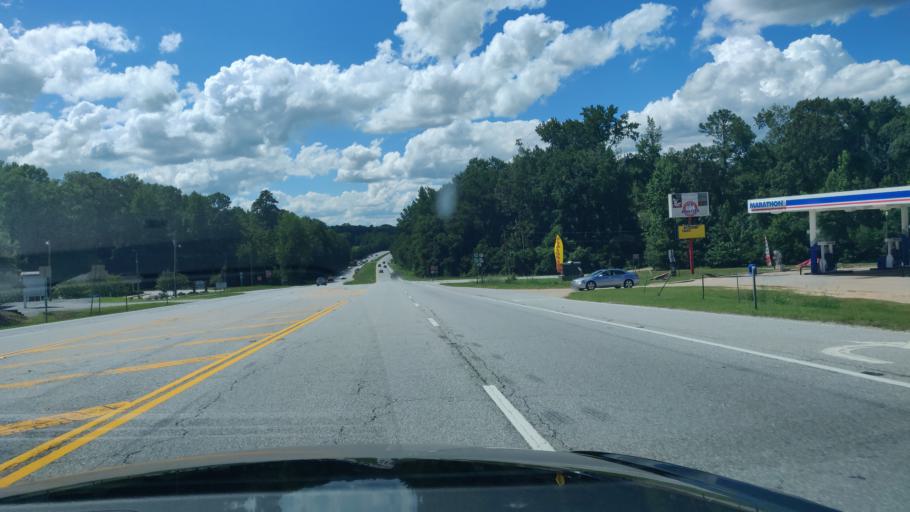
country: US
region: Georgia
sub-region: Chattahoochee County
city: Cusseta
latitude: 32.3080
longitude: -84.7922
